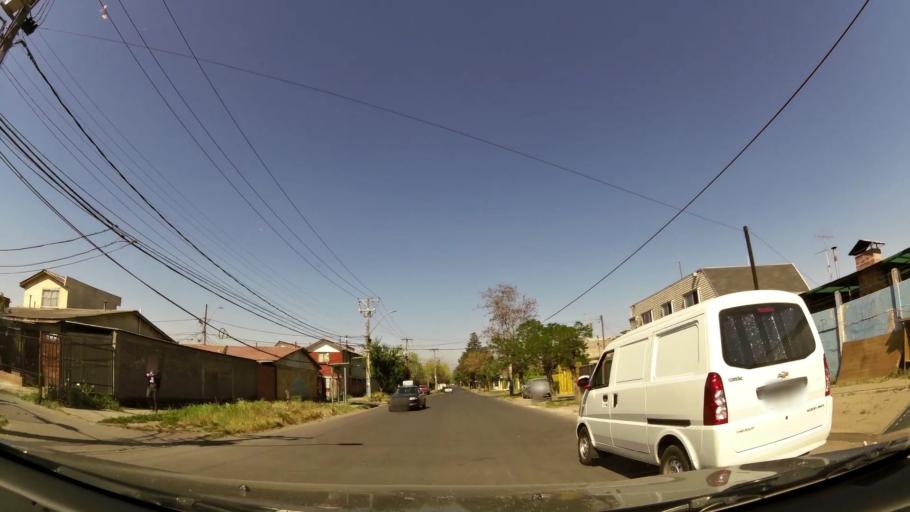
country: CL
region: Santiago Metropolitan
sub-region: Provincia de Maipo
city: San Bernardo
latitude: -33.6091
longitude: -70.7077
